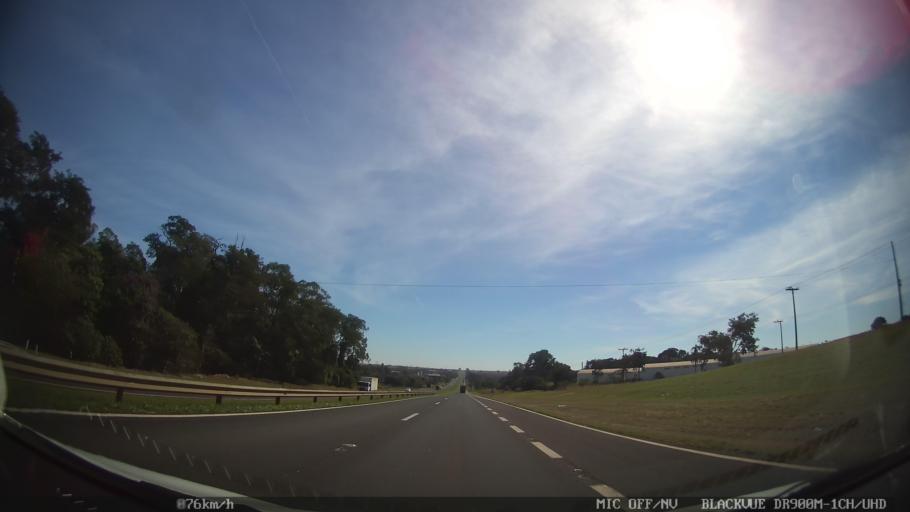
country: BR
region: Sao Paulo
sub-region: Pirassununga
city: Pirassununga
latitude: -22.0100
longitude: -47.4416
